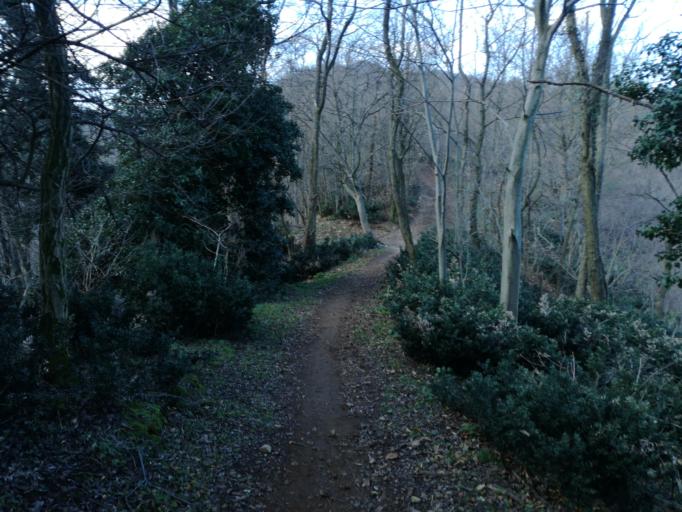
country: IT
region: Veneto
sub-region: Provincia di Padova
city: Galzignano
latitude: 45.2979
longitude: 11.7209
